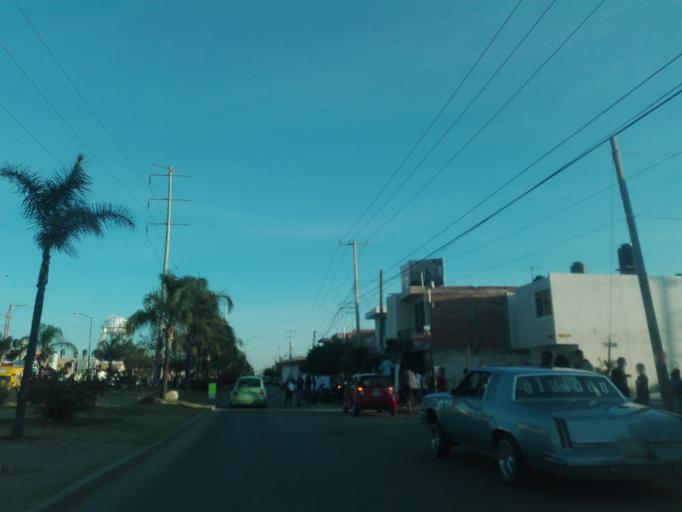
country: MX
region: Guanajuato
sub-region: Leon
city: Fraccionamiento Paraiso Real
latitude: 21.0787
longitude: -101.6206
